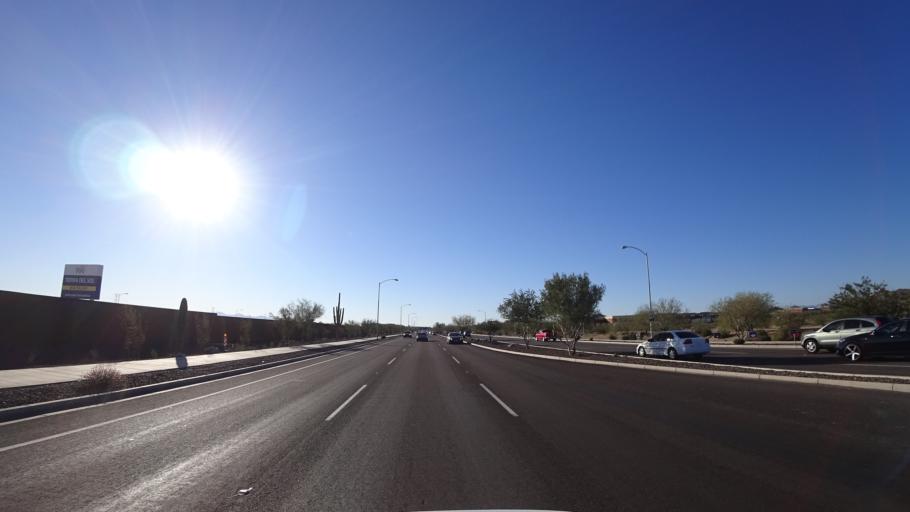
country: US
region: Arizona
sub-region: Maricopa County
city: Sun City West
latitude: 33.7106
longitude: -112.2646
